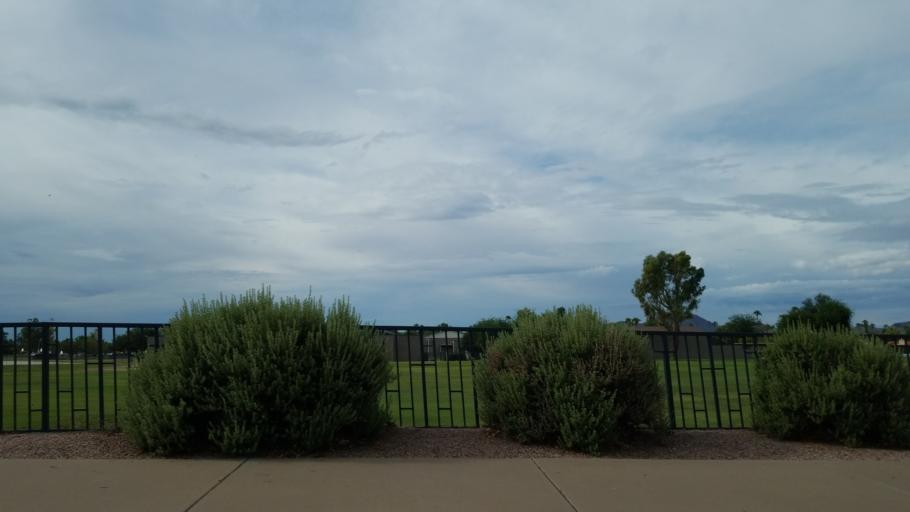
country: US
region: Arizona
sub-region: Maricopa County
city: Paradise Valley
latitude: 33.5726
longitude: -111.8974
